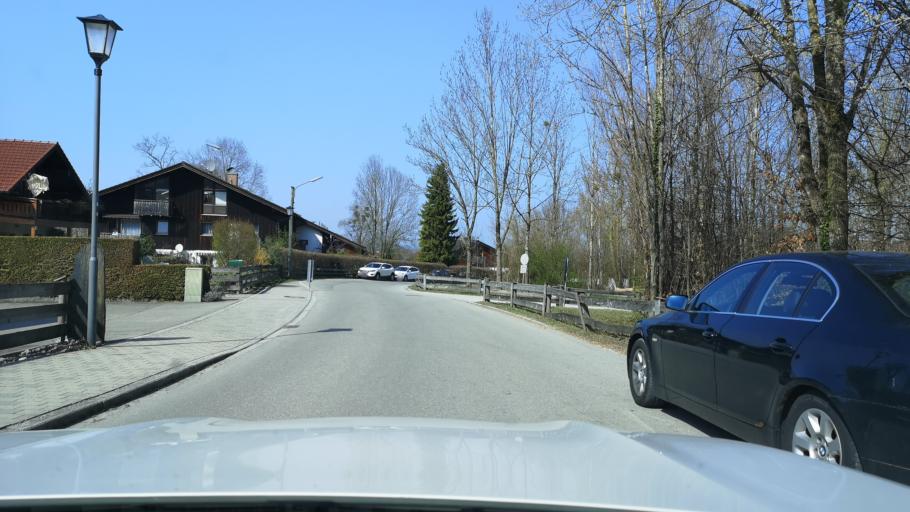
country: DE
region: Bavaria
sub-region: Upper Bavaria
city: Bad Feilnbach
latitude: 47.7663
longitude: 12.0134
